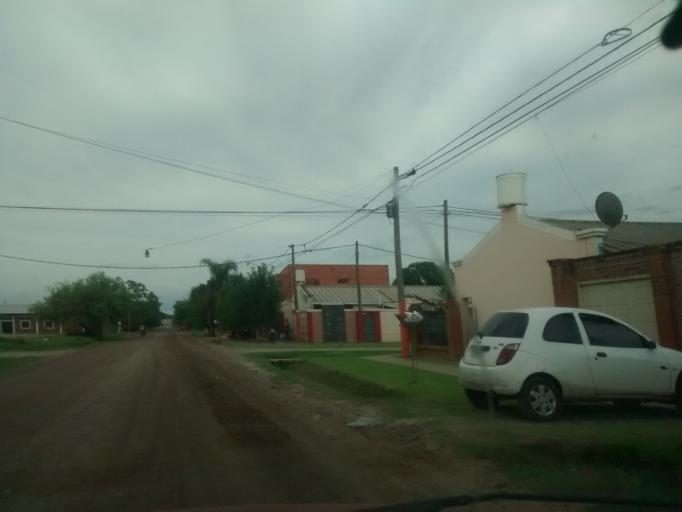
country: AR
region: Chaco
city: Fontana
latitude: -27.4564
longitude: -59.0319
